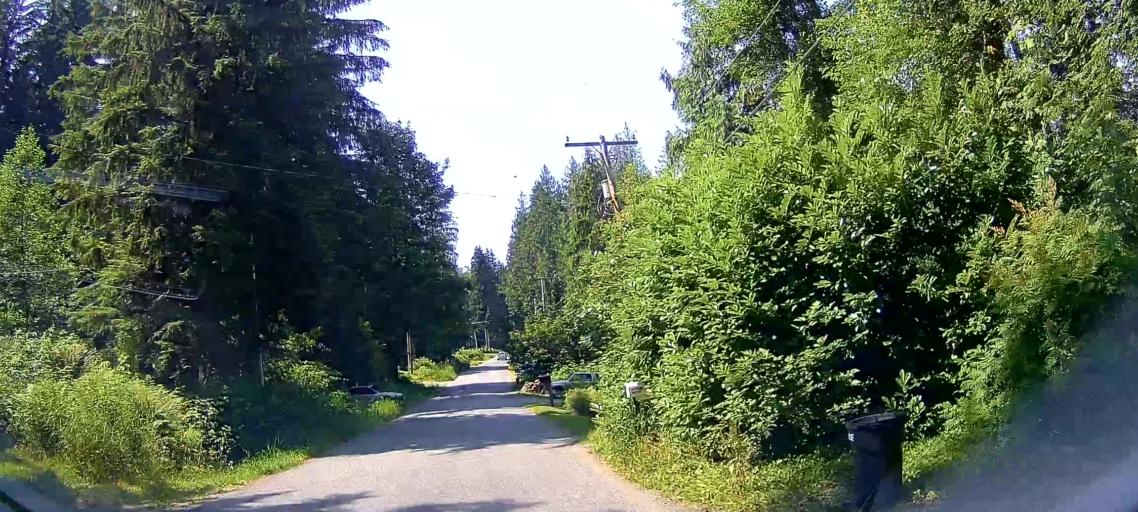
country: US
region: Washington
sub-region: Snohomish County
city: Arlington Heights
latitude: 48.3193
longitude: -122.0293
